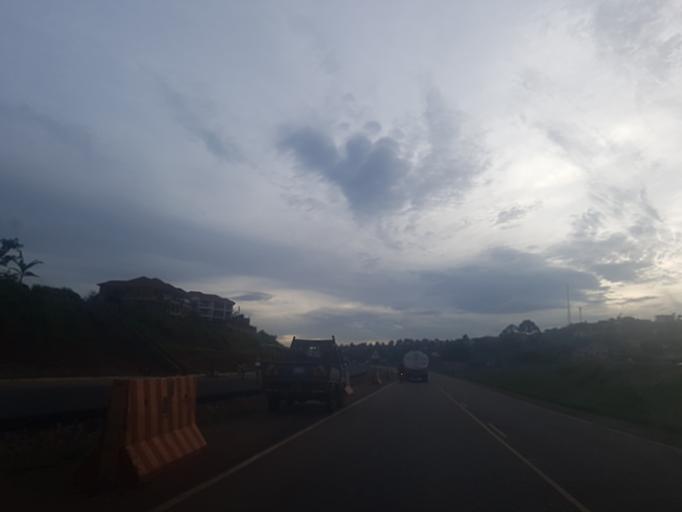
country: UG
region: Central Region
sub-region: Wakiso District
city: Kireka
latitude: 0.3688
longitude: 32.6173
